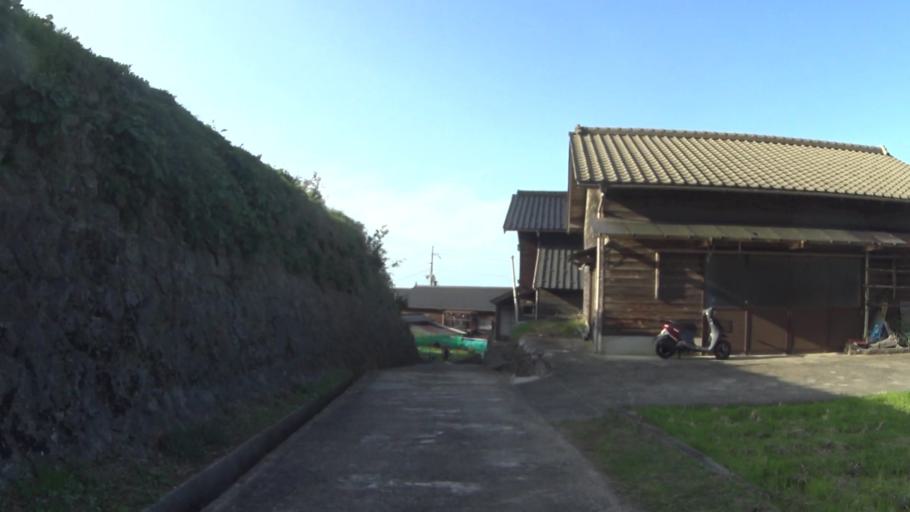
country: JP
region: Kyoto
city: Miyazu
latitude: 35.7627
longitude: 135.2063
